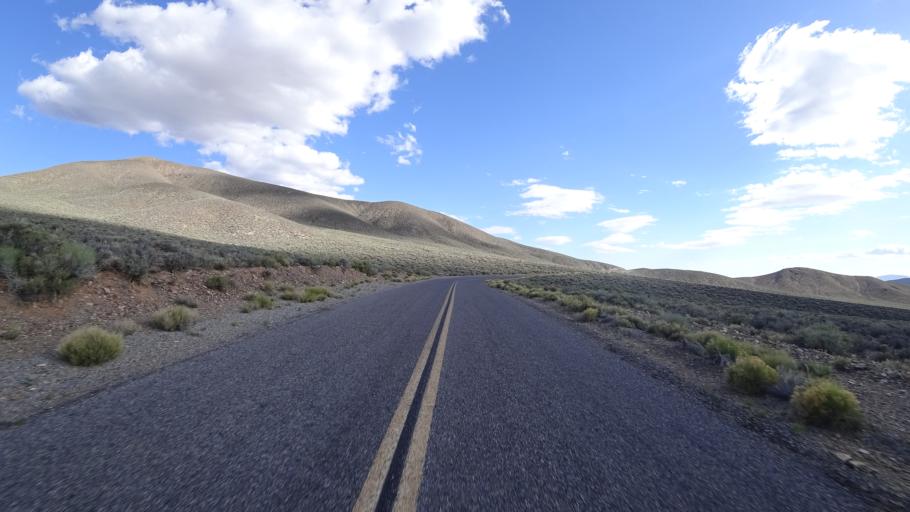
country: US
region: California
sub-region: San Bernardino County
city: Searles Valley
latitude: 36.3288
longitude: -117.1482
